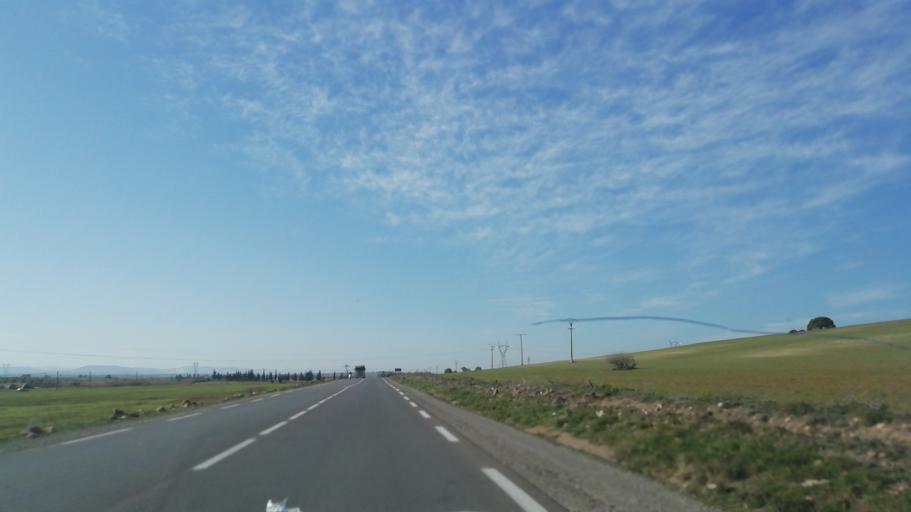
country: DZ
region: Tlemcen
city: Ouled Mimoun
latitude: 35.0476
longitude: -0.8349
